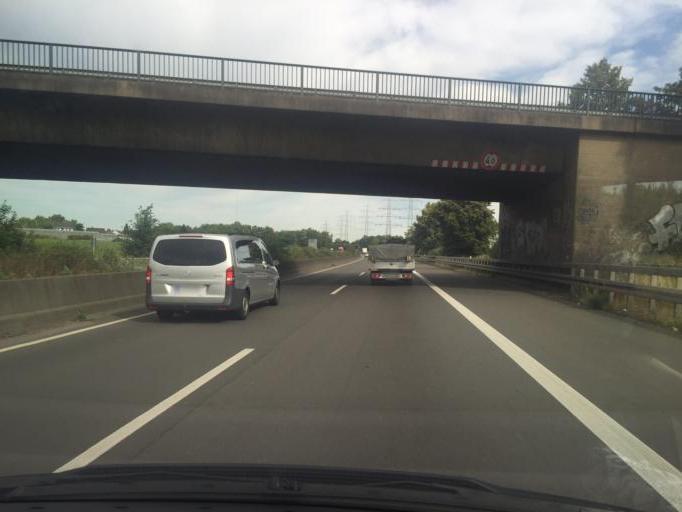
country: DE
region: North Rhine-Westphalia
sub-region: Regierungsbezirk Dusseldorf
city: Dormagen
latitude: 51.1295
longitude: 6.7921
